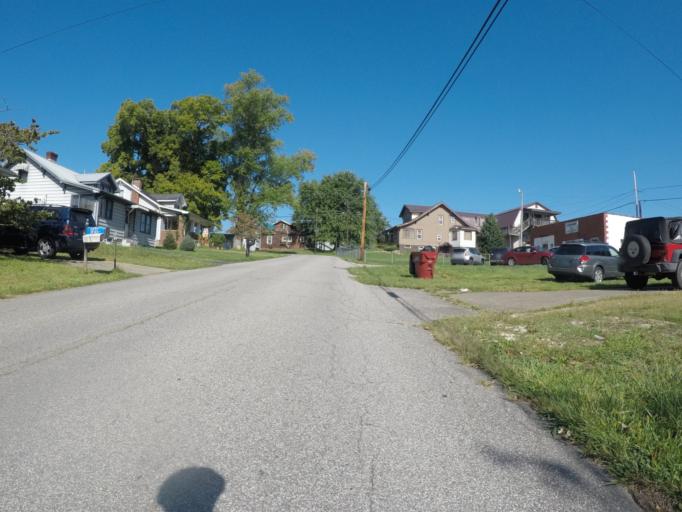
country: US
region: Kentucky
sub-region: Boyd County
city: Westwood
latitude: 38.4835
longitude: -82.6694
